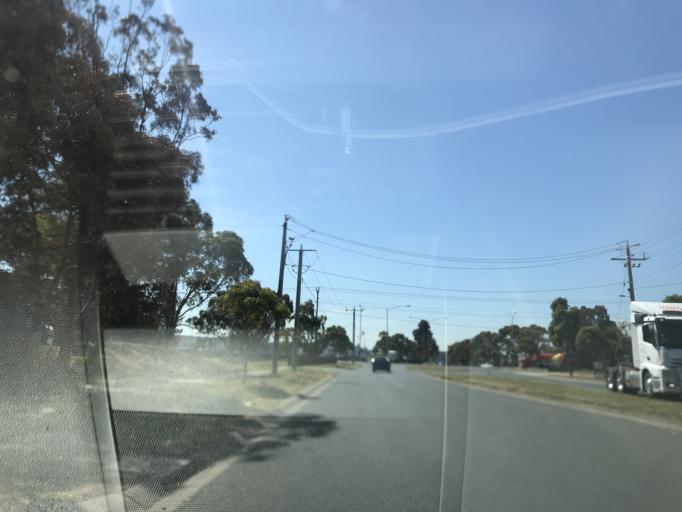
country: AU
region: Victoria
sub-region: Brimbank
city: Derrimut
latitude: -37.8144
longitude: 144.7822
